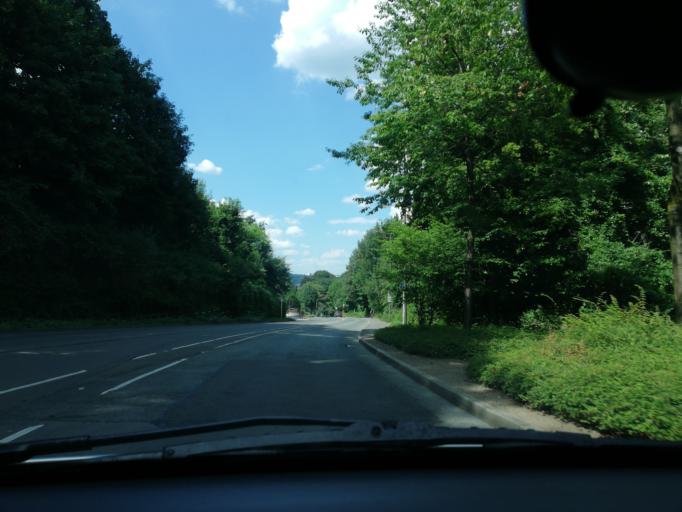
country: DE
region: North Rhine-Westphalia
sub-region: Regierungsbezirk Dusseldorf
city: Wuppertal
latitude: 51.2496
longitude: 7.1614
